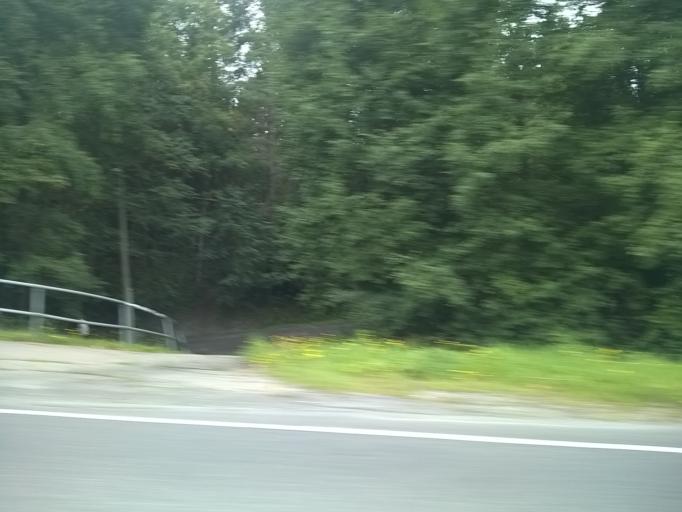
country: FI
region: Pirkanmaa
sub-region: Tampere
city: Tampere
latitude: 61.4652
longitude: 23.8417
